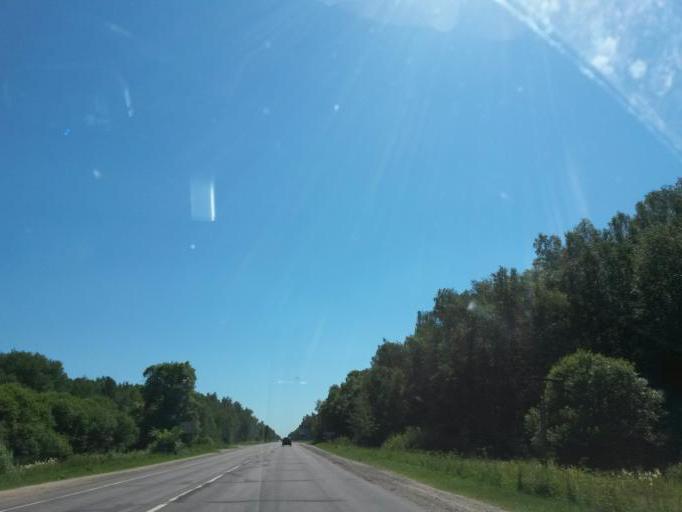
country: RU
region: Moskovskaya
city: Proletarskiy
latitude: 55.0632
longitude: 37.4356
